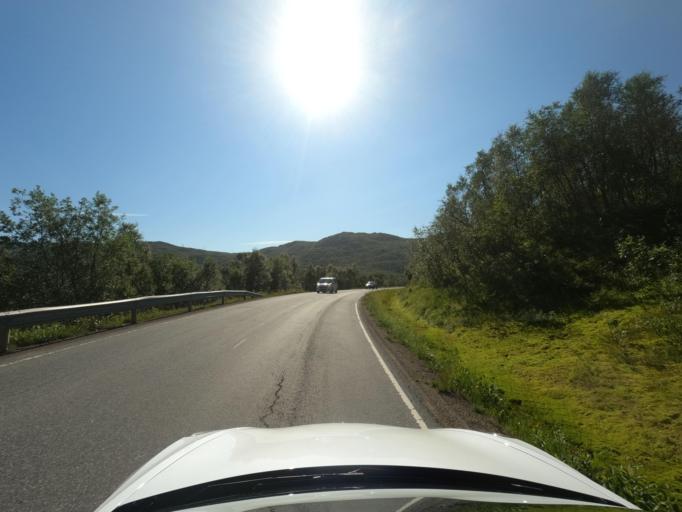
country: NO
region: Nordland
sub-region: Lodingen
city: Lodingen
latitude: 68.5542
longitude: 15.7509
